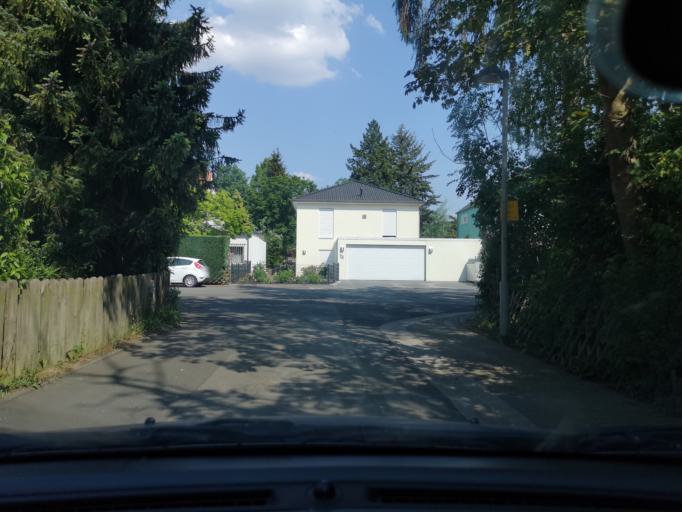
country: DE
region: Lower Saxony
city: Langenhagen
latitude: 52.4242
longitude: 9.7884
